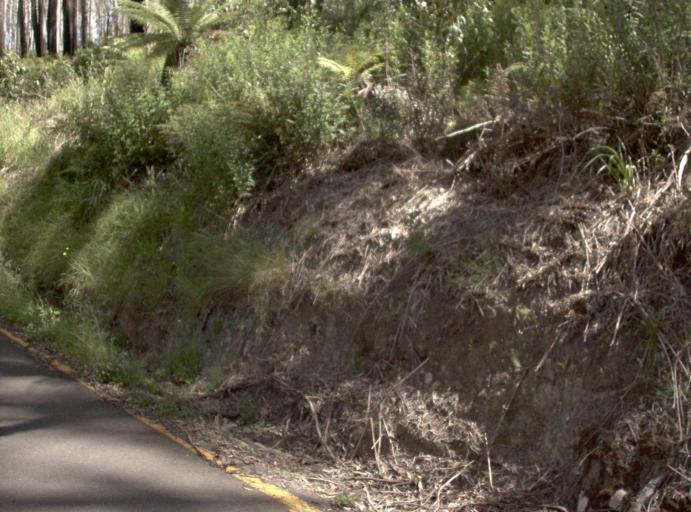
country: AU
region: Victoria
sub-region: Yarra Ranges
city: Millgrove
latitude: -37.5532
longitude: 145.8539
